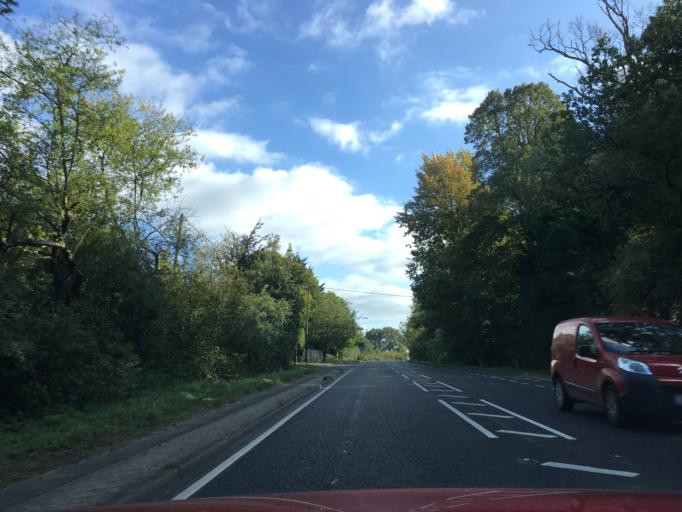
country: GB
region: England
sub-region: Hampshire
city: Tadley
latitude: 51.3165
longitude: -1.1194
